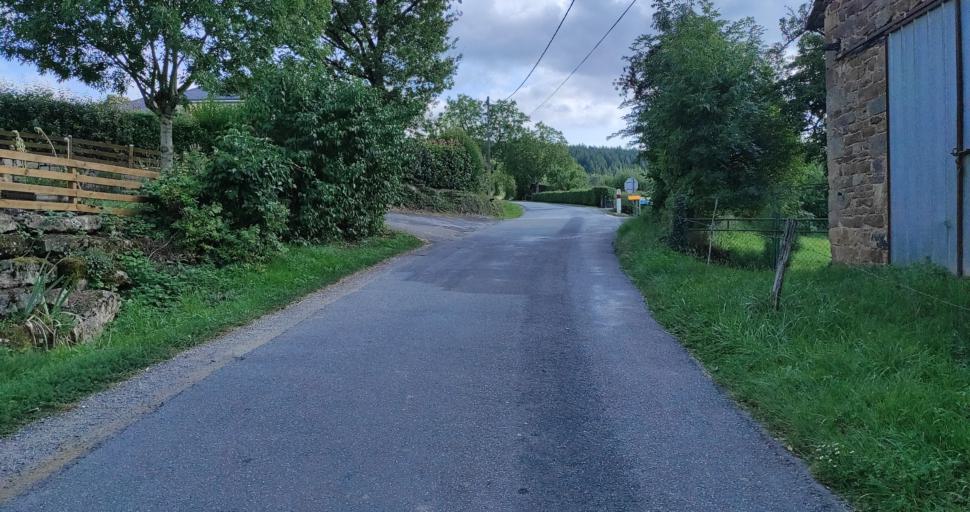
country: FR
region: Midi-Pyrenees
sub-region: Departement de l'Aveyron
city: La Loubiere
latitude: 44.3834
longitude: 2.7098
